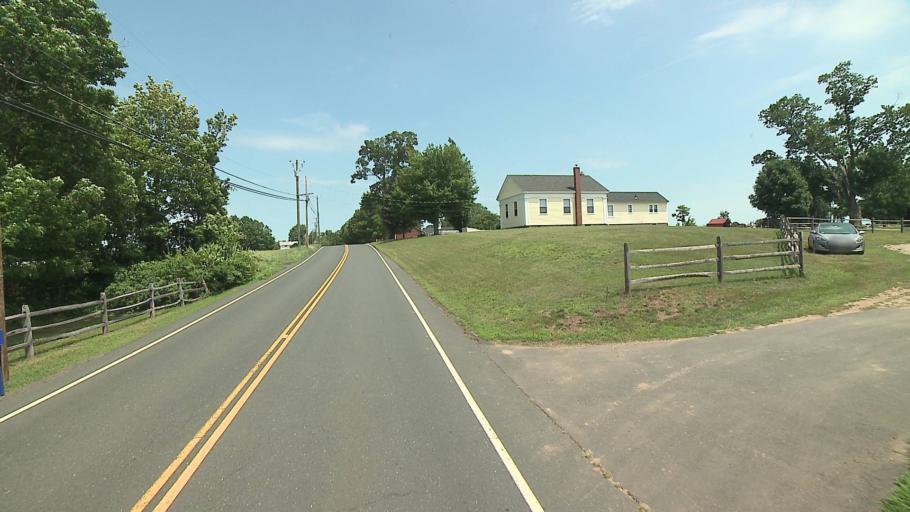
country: US
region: Connecticut
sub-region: Hartford County
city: Suffield Depot
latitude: 41.9751
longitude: -72.7024
